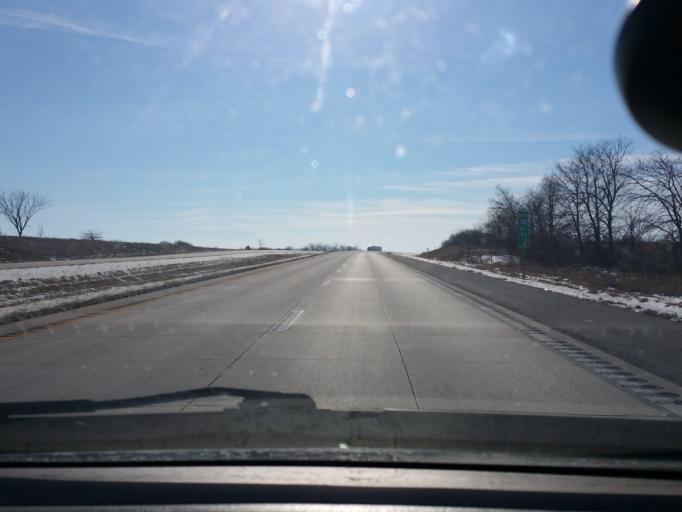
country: US
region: Missouri
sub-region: Daviess County
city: Gallatin
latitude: 39.9779
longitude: -94.0945
